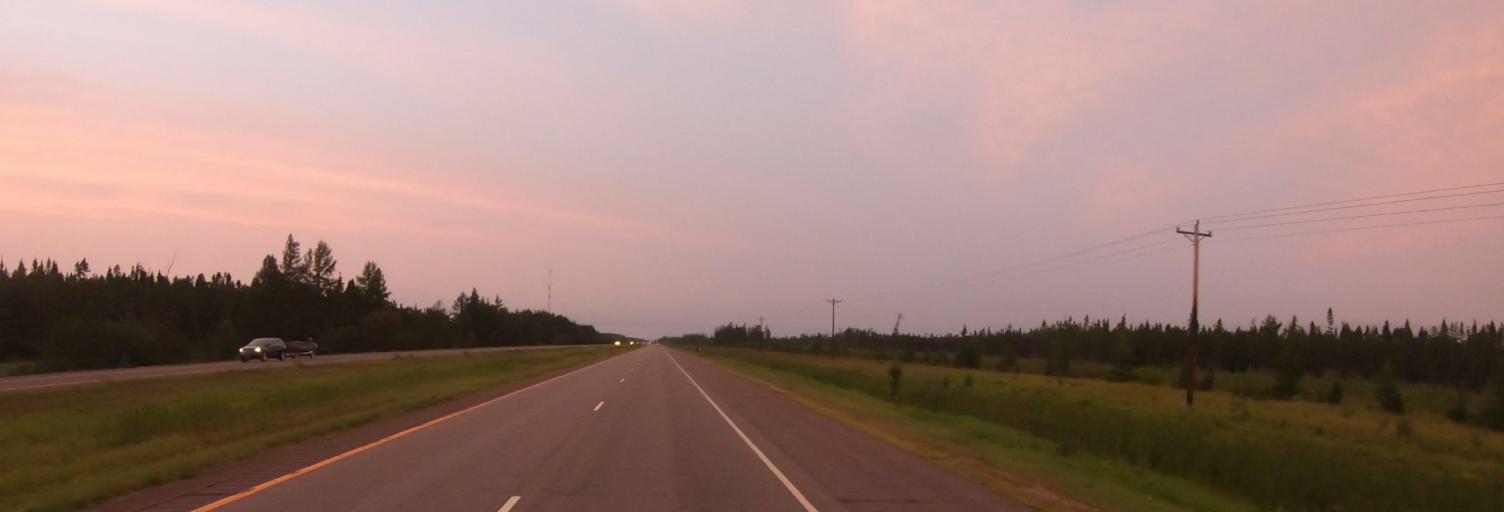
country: US
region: Minnesota
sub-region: Carlton County
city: Cloquet
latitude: 47.0561
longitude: -92.4708
